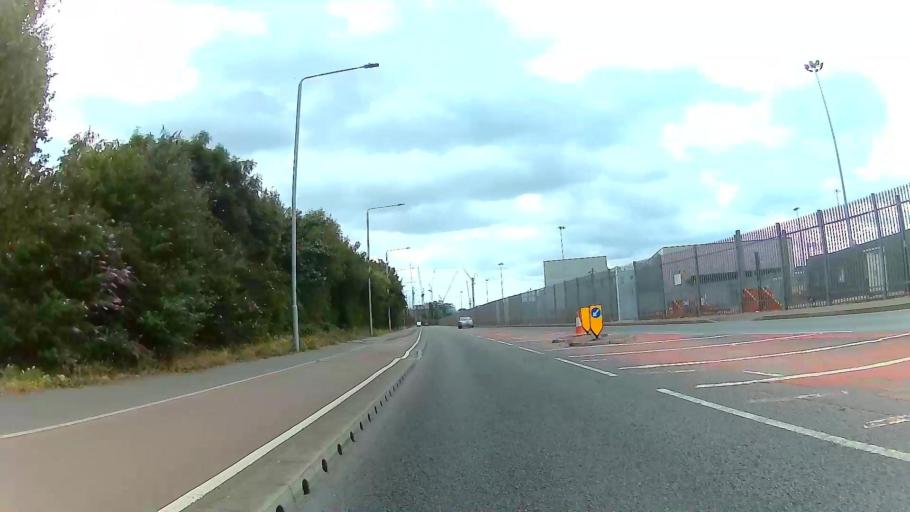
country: GB
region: England
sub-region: Greater London
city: Hackney
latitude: 51.5622
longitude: -0.0266
